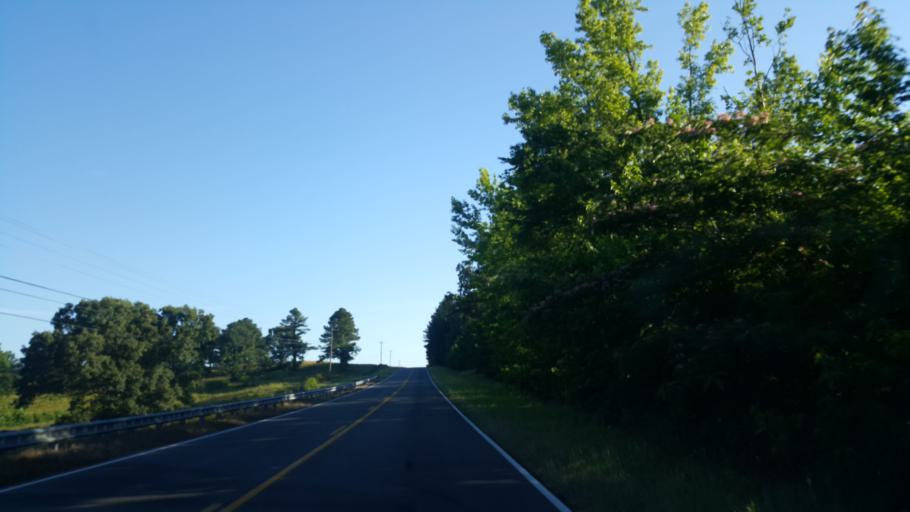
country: US
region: Tennessee
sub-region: Henderson County
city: Lexington
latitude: 35.5590
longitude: -88.3860
